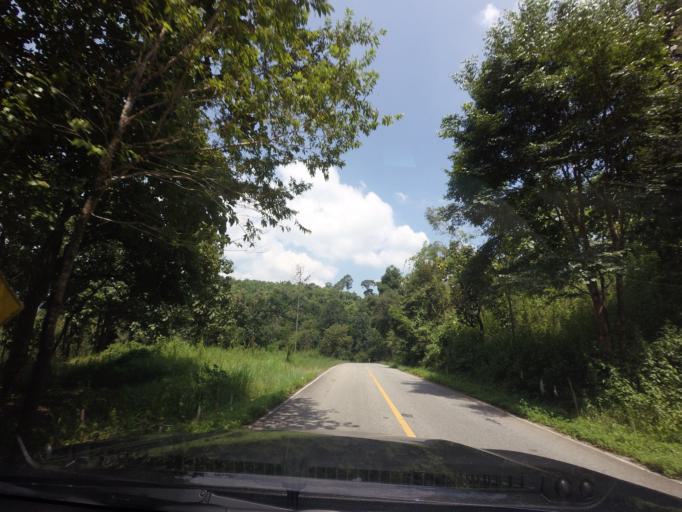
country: TH
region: Loei
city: Na Haeo
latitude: 17.6280
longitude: 100.9051
